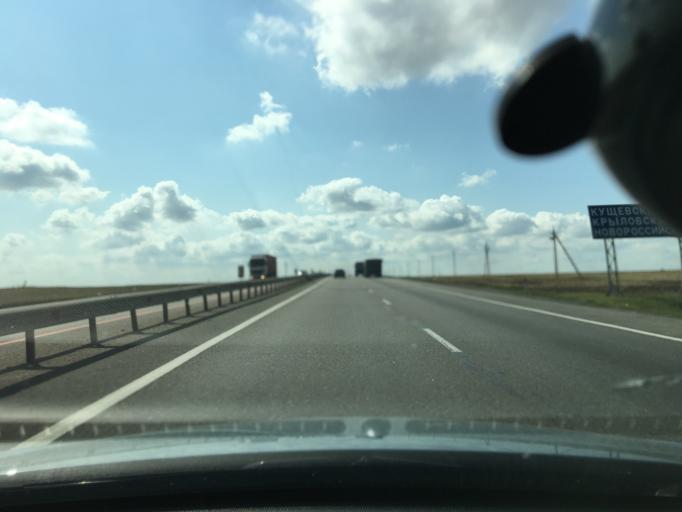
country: RU
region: Krasnodarskiy
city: Krasnoye
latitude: 46.7260
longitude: 39.6553
